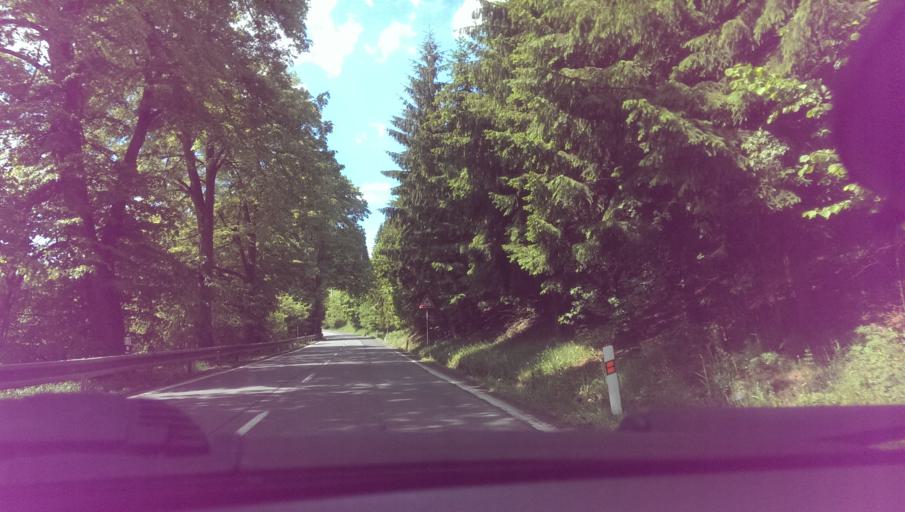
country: CZ
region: Zlin
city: Valasska Polanka
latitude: 49.2438
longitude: 17.9791
